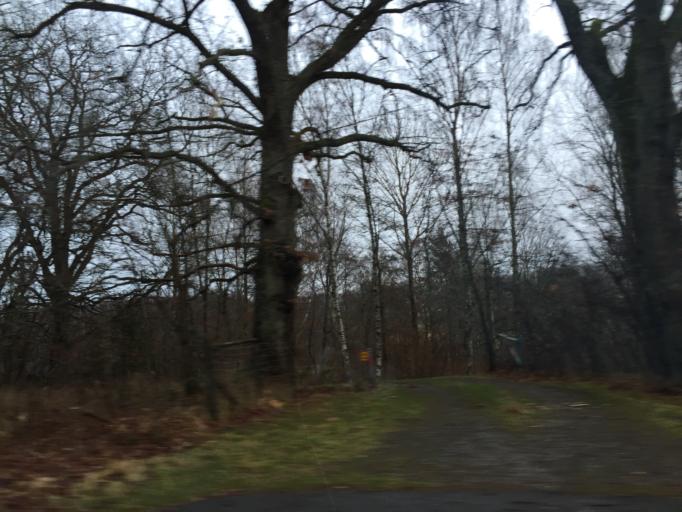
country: SE
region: Stockholm
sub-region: Nynashamns Kommun
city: Osmo
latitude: 59.0307
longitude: 17.9882
